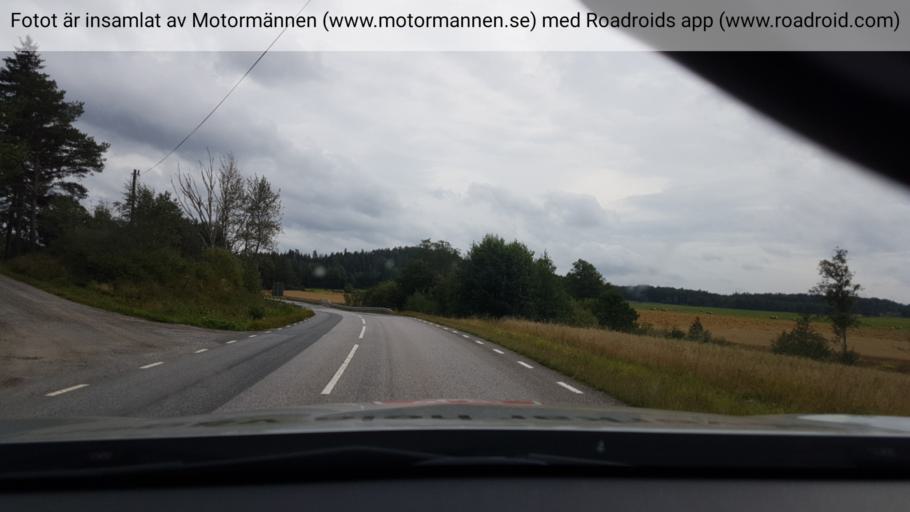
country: SE
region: Vaestra Goetaland
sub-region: Sotenas Kommun
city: Hunnebostrand
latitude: 58.5569
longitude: 11.4023
